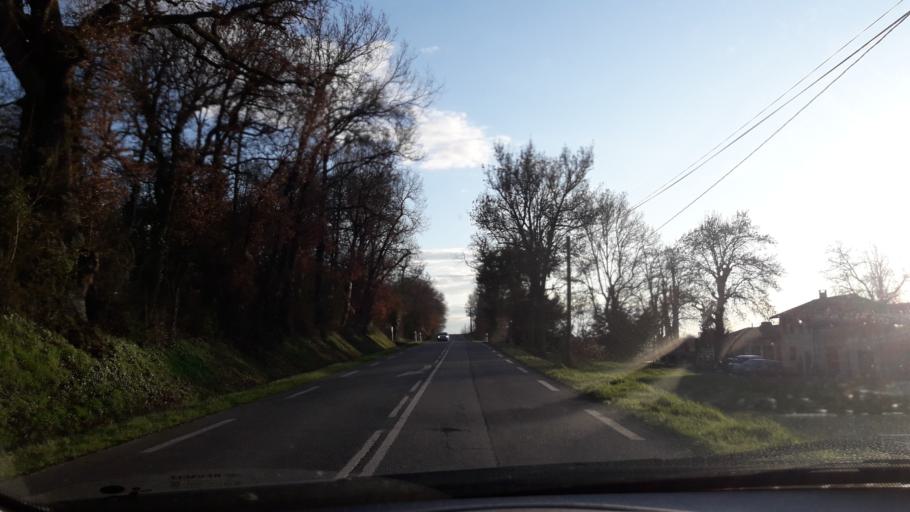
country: FR
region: Midi-Pyrenees
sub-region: Departement de la Haute-Garonne
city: Montaigut-sur-Save
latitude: 43.7105
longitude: 1.2462
